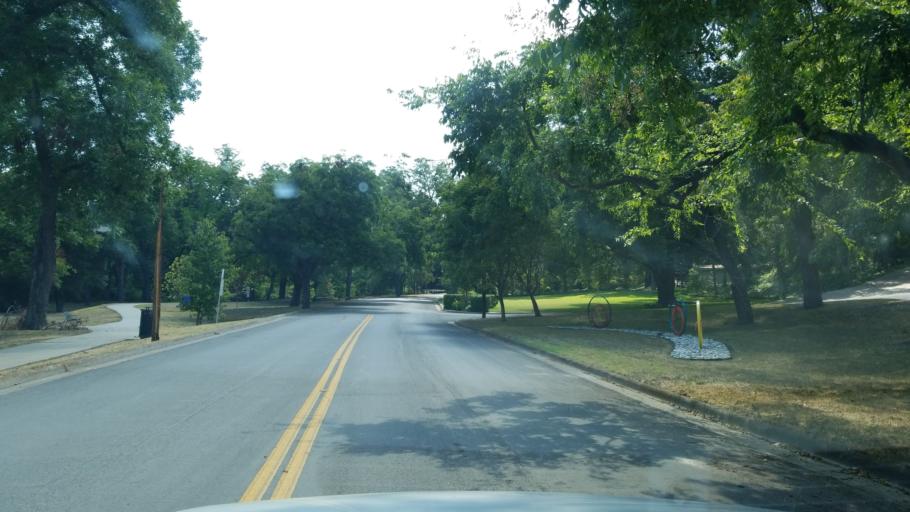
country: US
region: Texas
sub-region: Dallas County
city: Dallas
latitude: 32.7670
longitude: -96.8298
